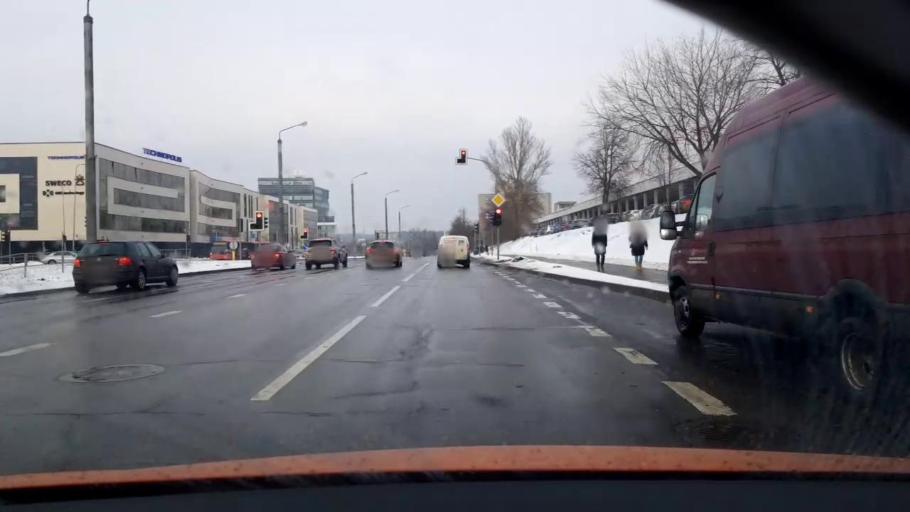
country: LT
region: Vilnius County
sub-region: Vilnius
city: Vilnius
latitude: 54.7164
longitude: 25.2869
